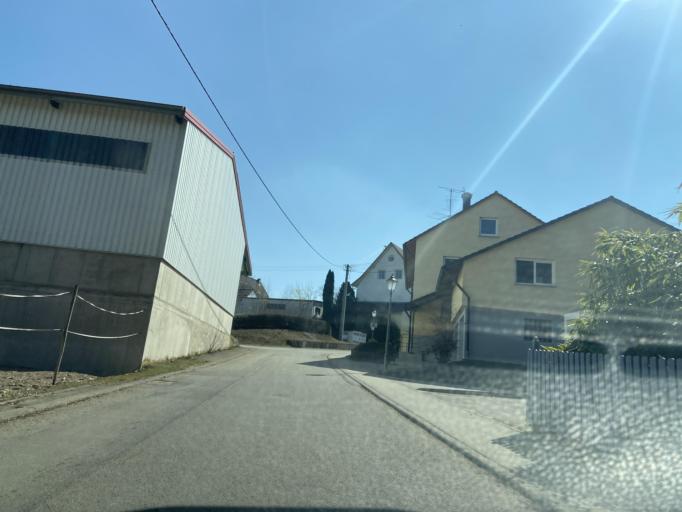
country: DE
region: Baden-Wuerttemberg
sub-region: Tuebingen Region
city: Inzigkofen
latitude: 48.0730
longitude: 9.1785
